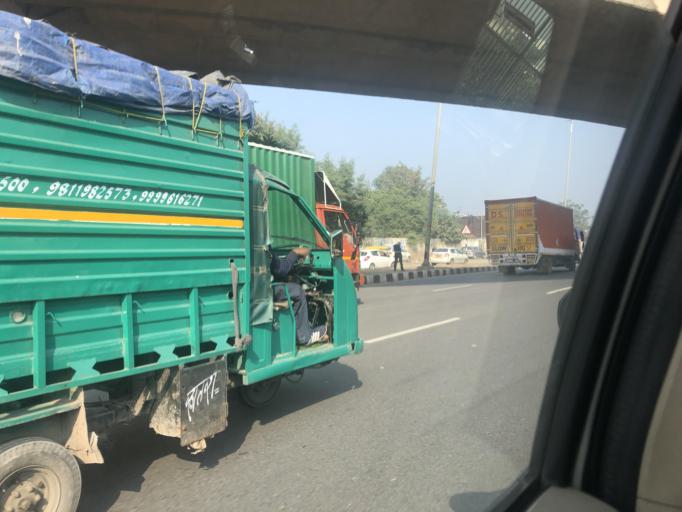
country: IN
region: Haryana
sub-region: Gurgaon
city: Gurgaon
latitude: 28.5397
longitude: 77.1168
